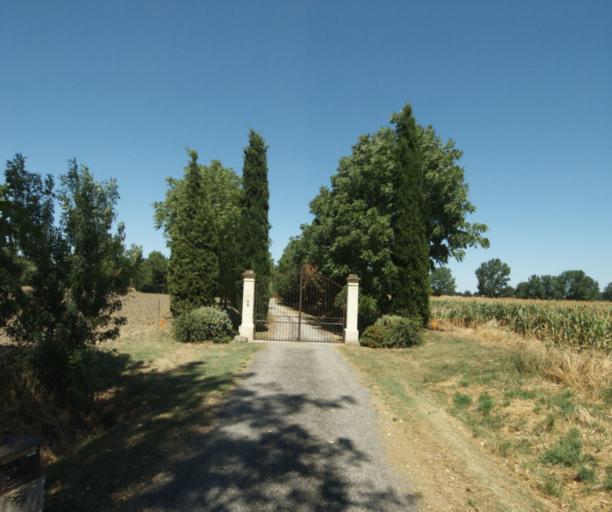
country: FR
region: Midi-Pyrenees
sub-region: Departement de la Haute-Garonne
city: Saint-Felix-Lauragais
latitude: 43.4668
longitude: 1.9311
